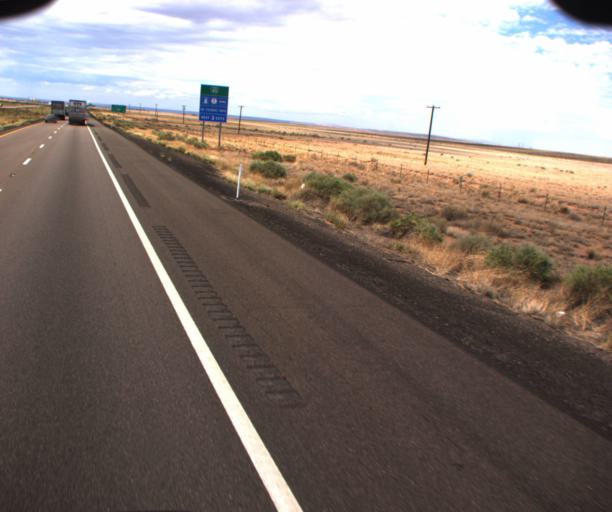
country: US
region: Arizona
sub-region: Navajo County
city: Holbrook
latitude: 34.9598
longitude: -110.1070
